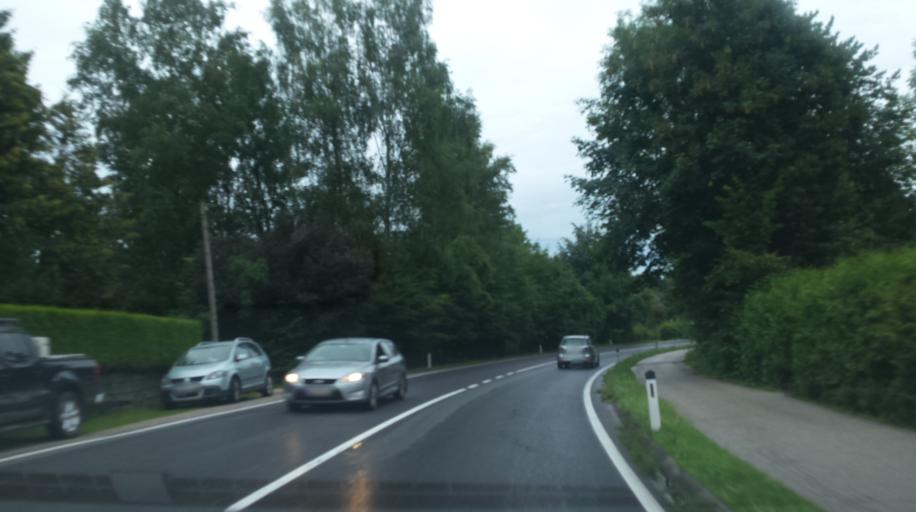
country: AT
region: Upper Austria
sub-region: Politischer Bezirk Gmunden
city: Altmunster
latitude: 47.8637
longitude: 13.7764
